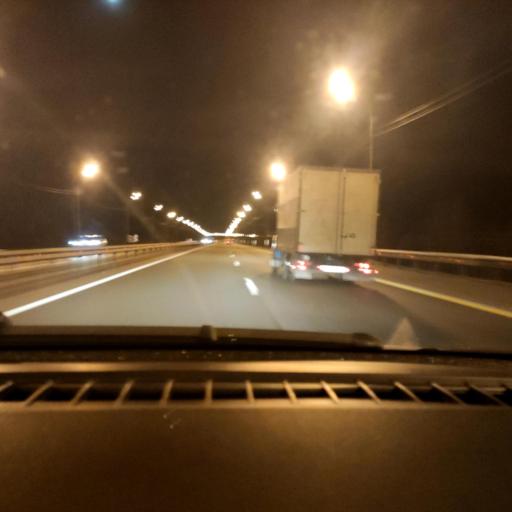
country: RU
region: Lipetsk
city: Khlevnoye
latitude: 52.1902
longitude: 39.1792
